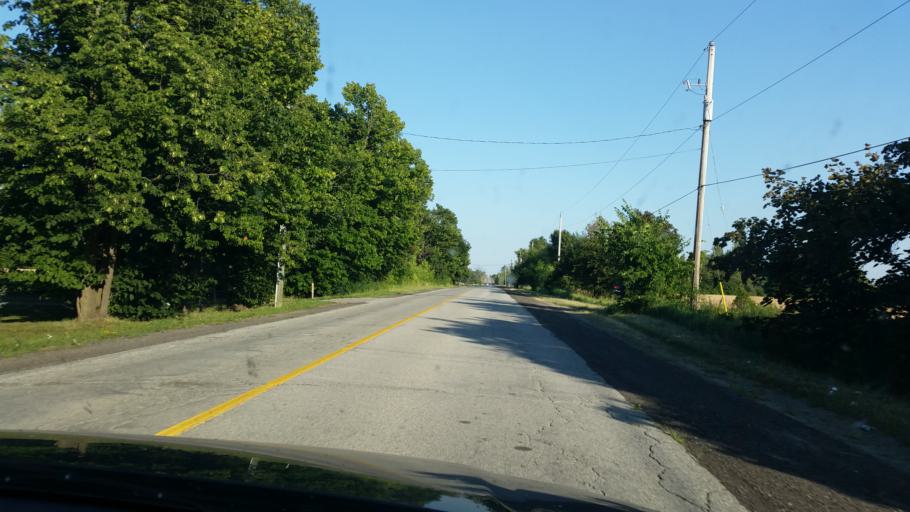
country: CA
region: Ontario
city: Brampton
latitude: 43.7896
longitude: -79.8530
